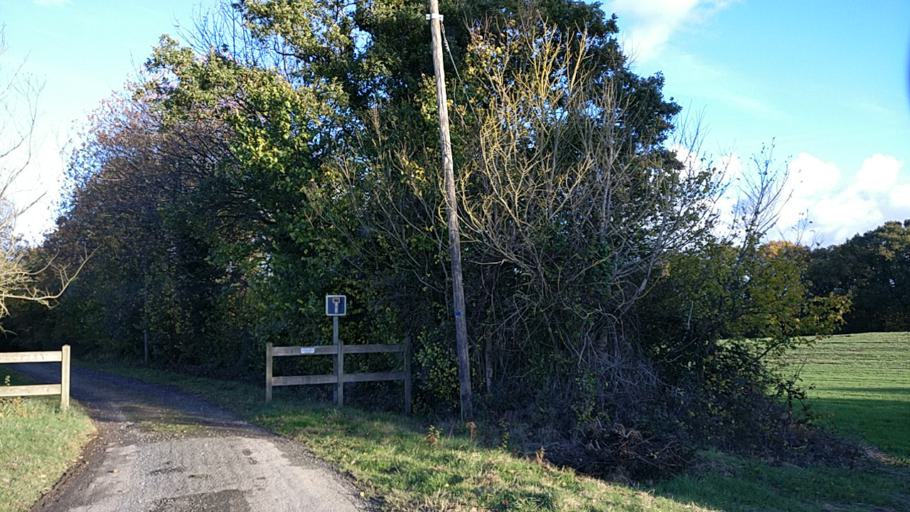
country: FR
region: Brittany
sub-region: Departement d'Ille-et-Vilaine
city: Cesson-Sevigne
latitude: 48.1349
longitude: -1.5898
